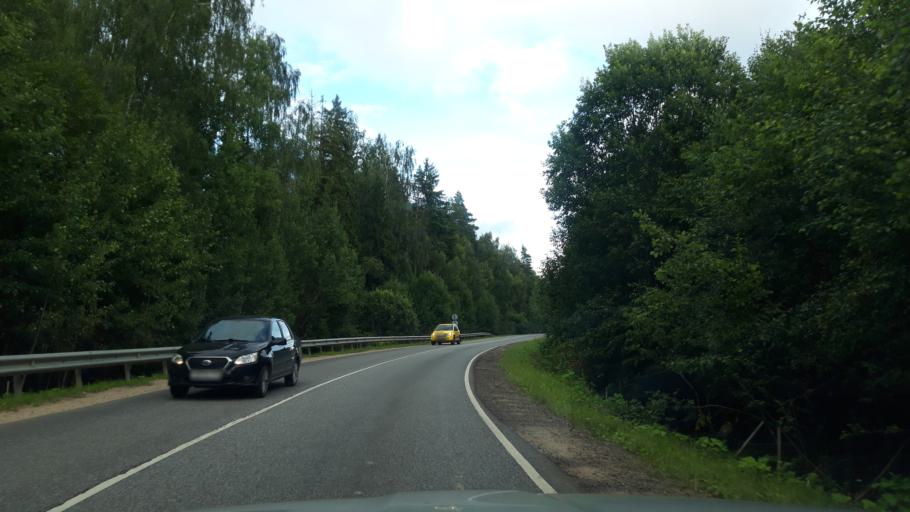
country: RU
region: Moskovskaya
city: Solnechnogorsk
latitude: 56.0965
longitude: 36.8509
